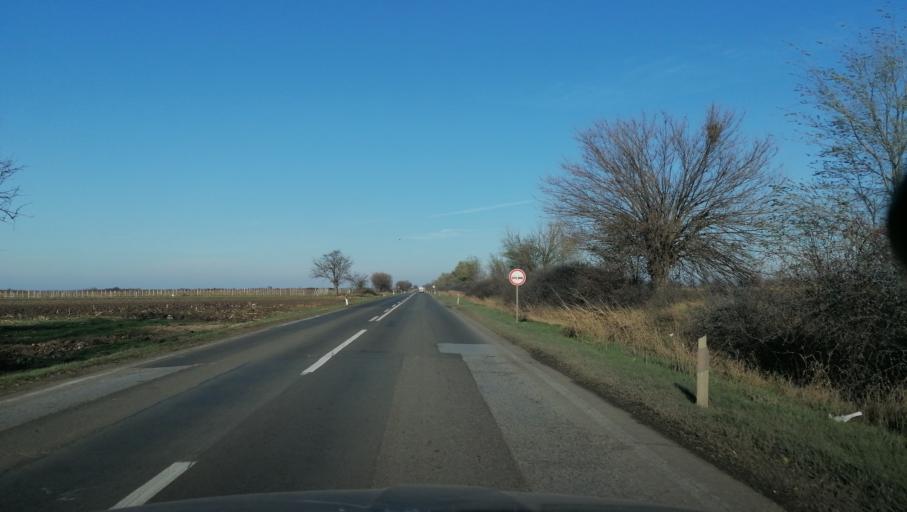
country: RS
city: Centa
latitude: 45.1368
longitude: 20.3902
